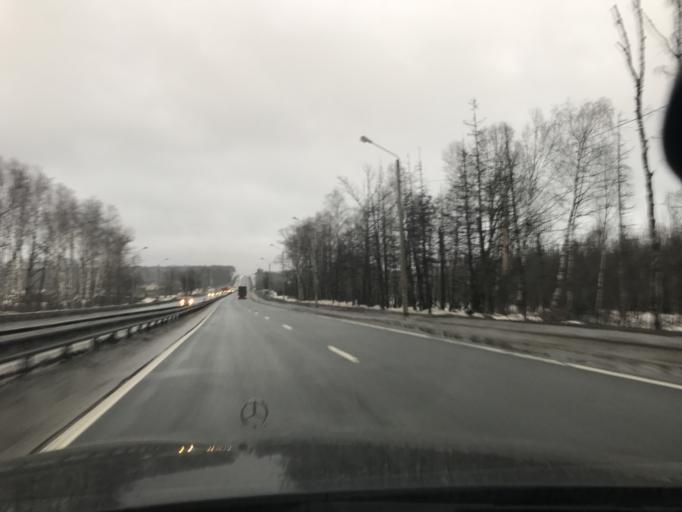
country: RU
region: Vladimir
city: Melekhovo
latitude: 56.2098
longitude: 41.2744
